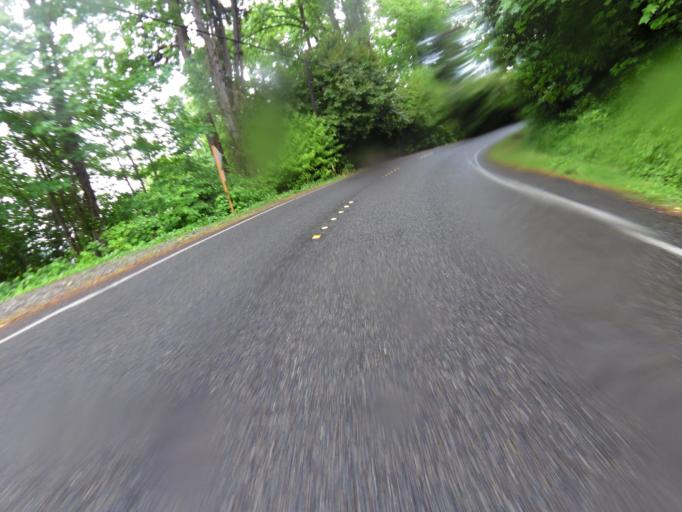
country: US
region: Washington
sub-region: King County
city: Bryn Mawr-Skyway
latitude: 47.5260
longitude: -122.2269
